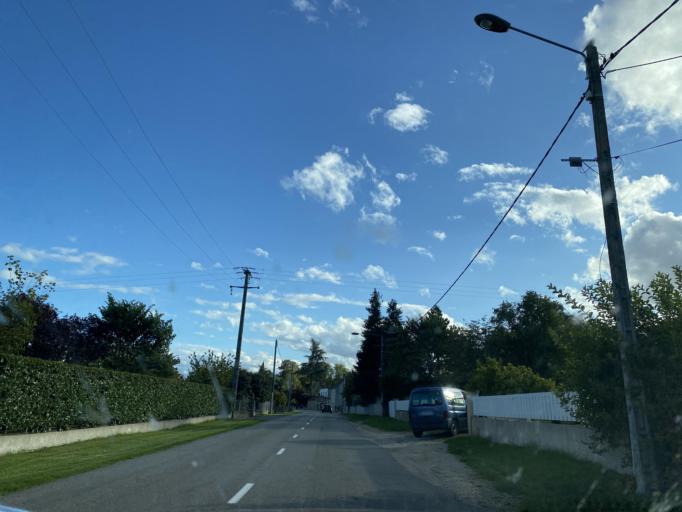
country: FR
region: Auvergne
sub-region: Departement de l'Allier
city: Gannat
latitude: 46.0824
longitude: 3.2705
